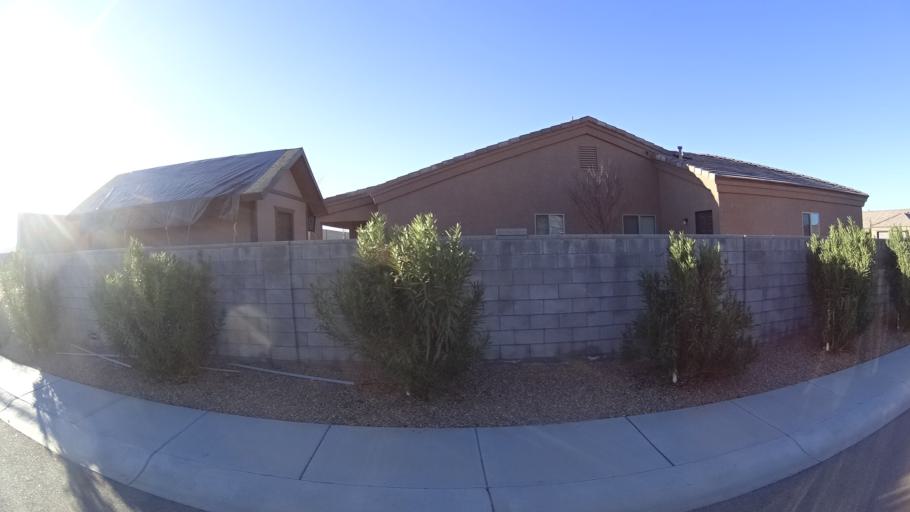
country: US
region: Arizona
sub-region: Mohave County
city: New Kingman-Butler
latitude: 35.2230
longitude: -113.9909
